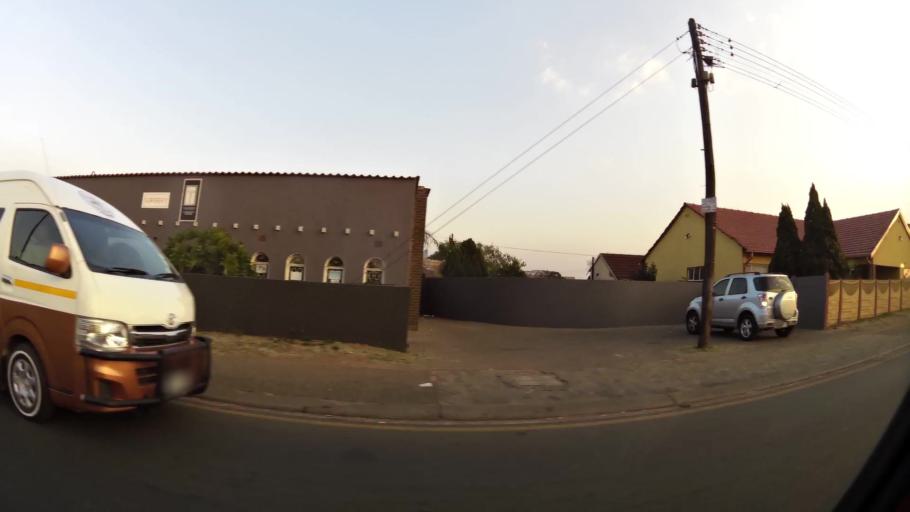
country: ZA
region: Gauteng
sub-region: City of Johannesburg Metropolitan Municipality
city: Soweto
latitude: -26.2919
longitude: 27.8998
